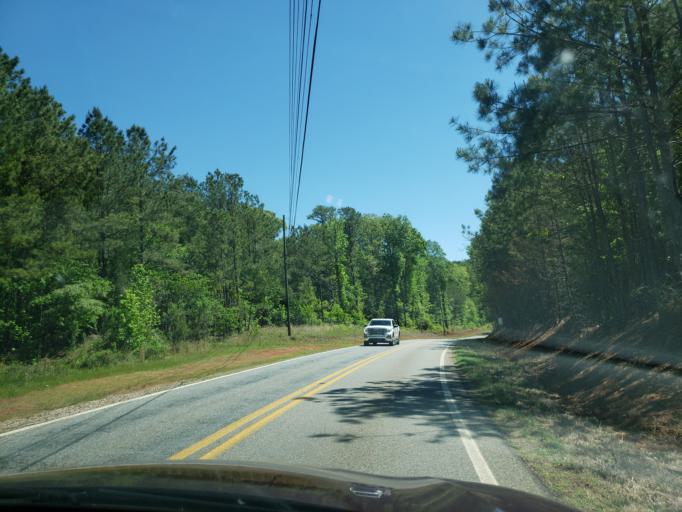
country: US
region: Alabama
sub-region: Tallapoosa County
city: Dadeville
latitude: 32.7067
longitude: -85.8353
